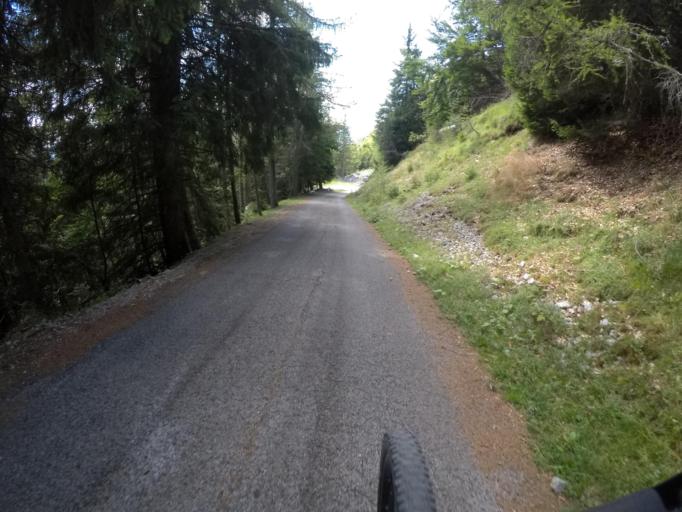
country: IT
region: Friuli Venezia Giulia
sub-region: Provincia di Udine
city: Ligosullo
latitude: 46.5002
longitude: 13.0676
